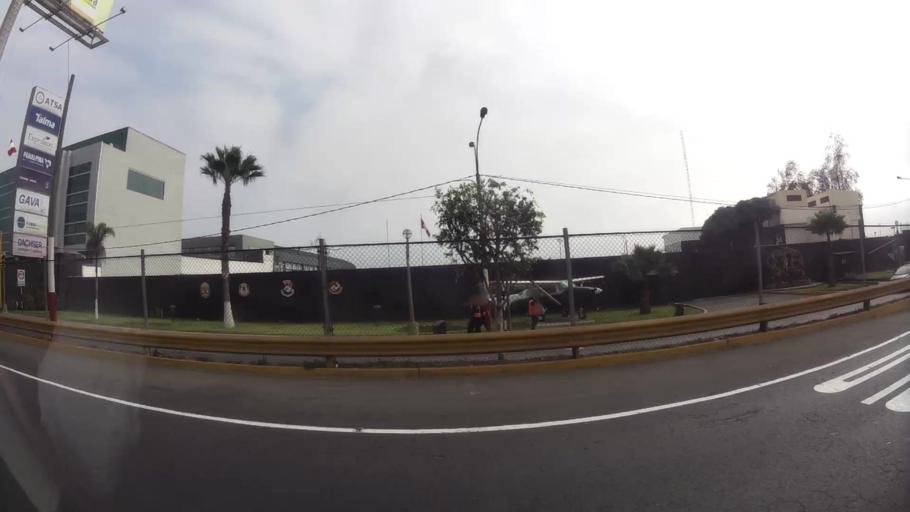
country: PE
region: Callao
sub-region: Callao
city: Callao
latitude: -12.0272
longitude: -77.1034
